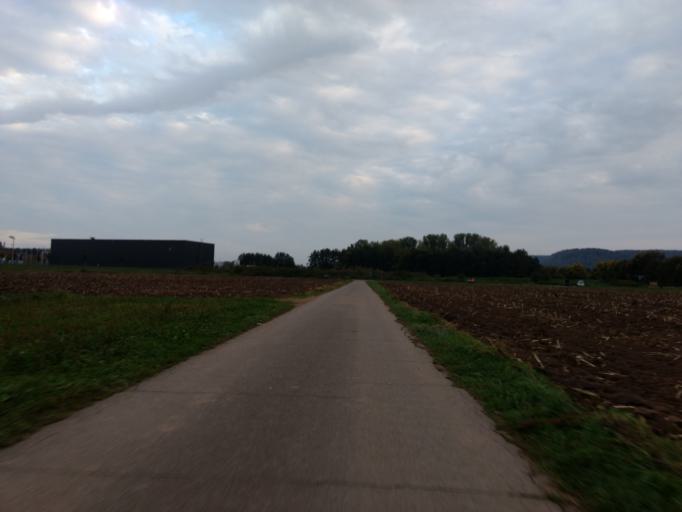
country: DE
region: Saarland
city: Rehlingen-Siersburg
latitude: 49.3752
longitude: 6.7013
